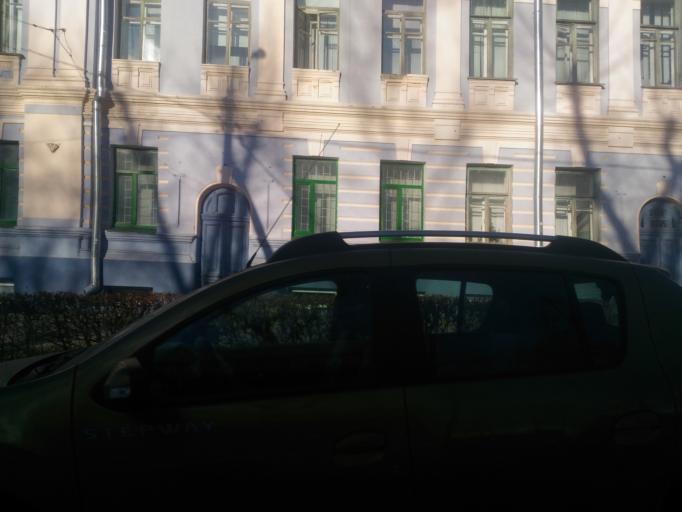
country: RU
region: Ulyanovsk
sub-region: Ulyanovskiy Rayon
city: Ulyanovsk
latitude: 54.3106
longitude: 48.3802
